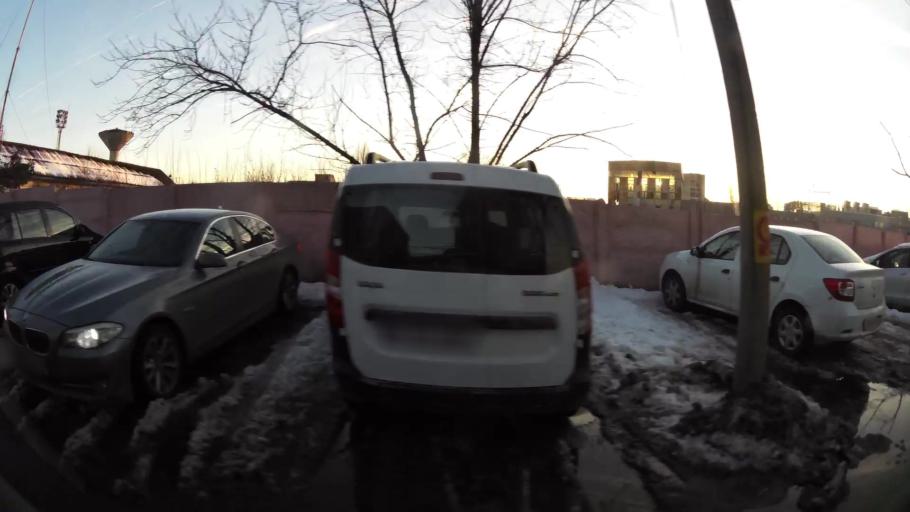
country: RO
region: Ilfov
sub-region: Comuna Fundeni-Dobroesti
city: Fundeni
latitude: 44.4524
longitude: 26.1347
